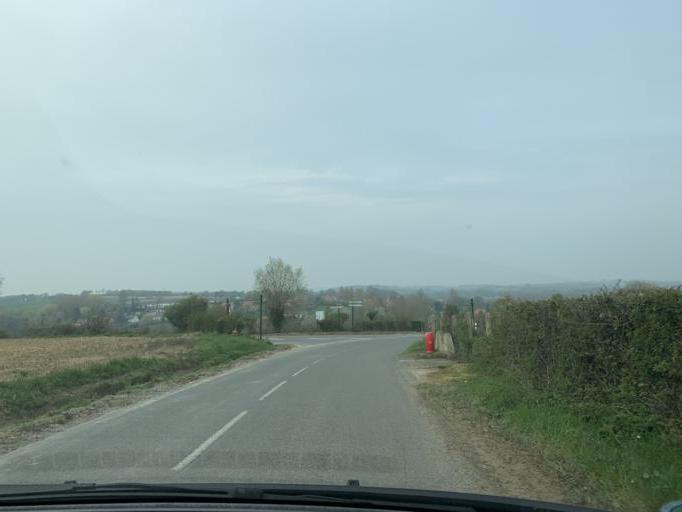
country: FR
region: Nord-Pas-de-Calais
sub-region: Departement du Pas-de-Calais
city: Longfosse
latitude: 50.6979
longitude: 1.7771
